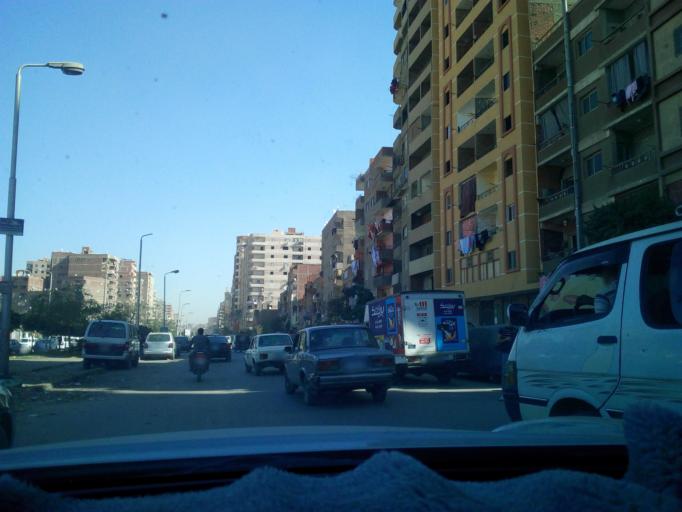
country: EG
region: Muhafazat al Qalyubiyah
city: Al Khankah
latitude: 30.1414
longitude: 31.3366
